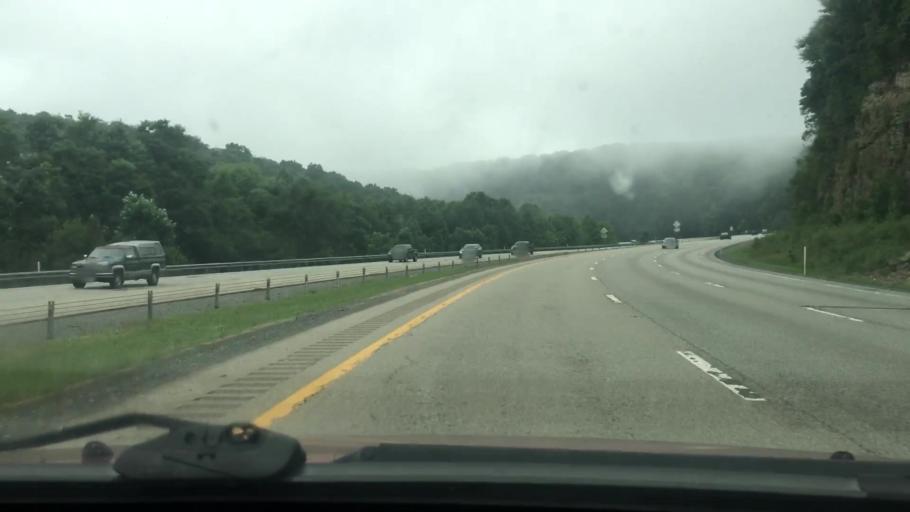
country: US
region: West Virginia
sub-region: Monongalia County
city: Cheat Lake
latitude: 39.6612
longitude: -79.8164
